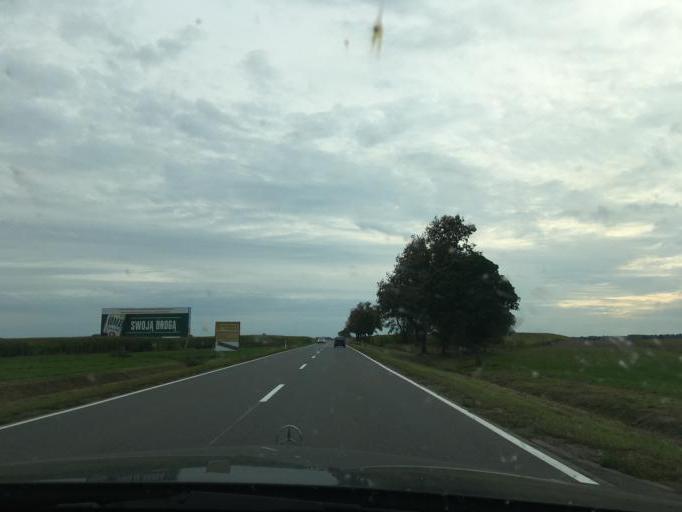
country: PL
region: Masovian Voivodeship
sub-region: Powiat ostrolecki
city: Czerwin
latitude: 52.9491
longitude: 21.8887
